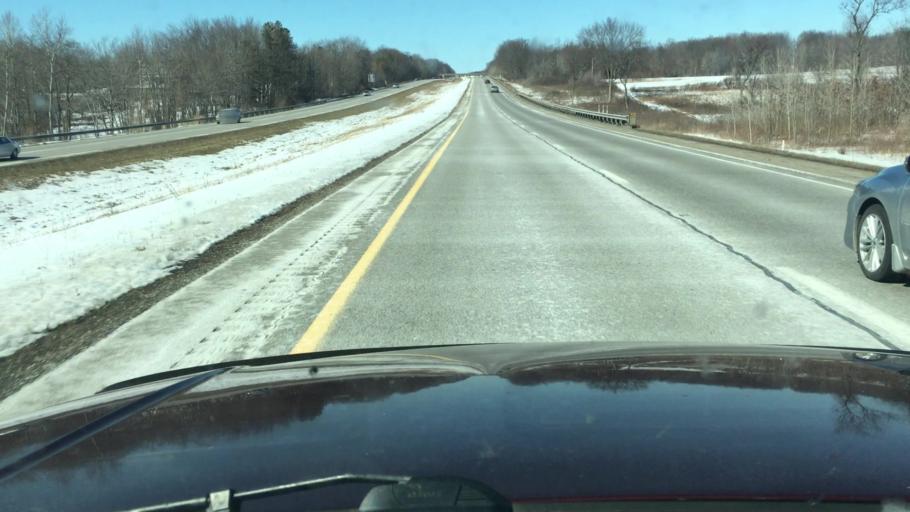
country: US
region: Pennsylvania
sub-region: Crawford County
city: Cochranton
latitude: 41.4714
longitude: -80.1669
